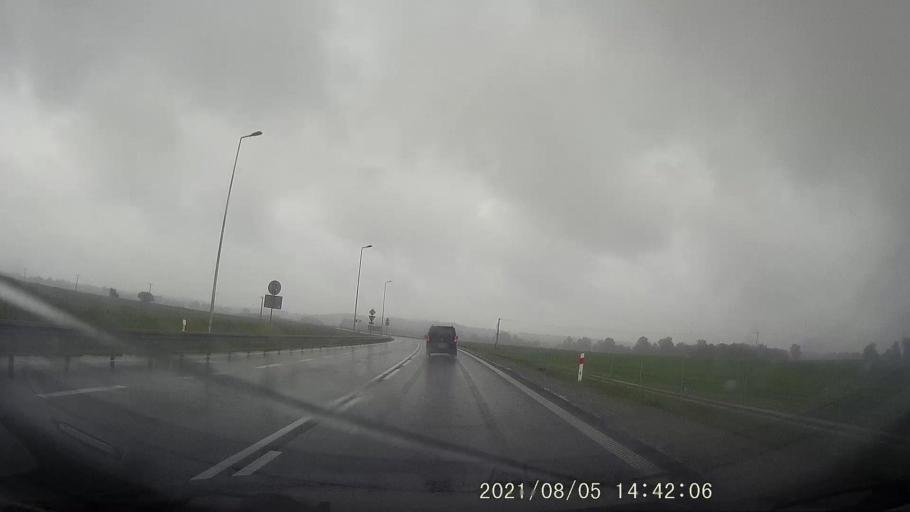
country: PL
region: Opole Voivodeship
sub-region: Powiat nyski
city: Nysa
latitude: 50.4715
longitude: 17.4063
